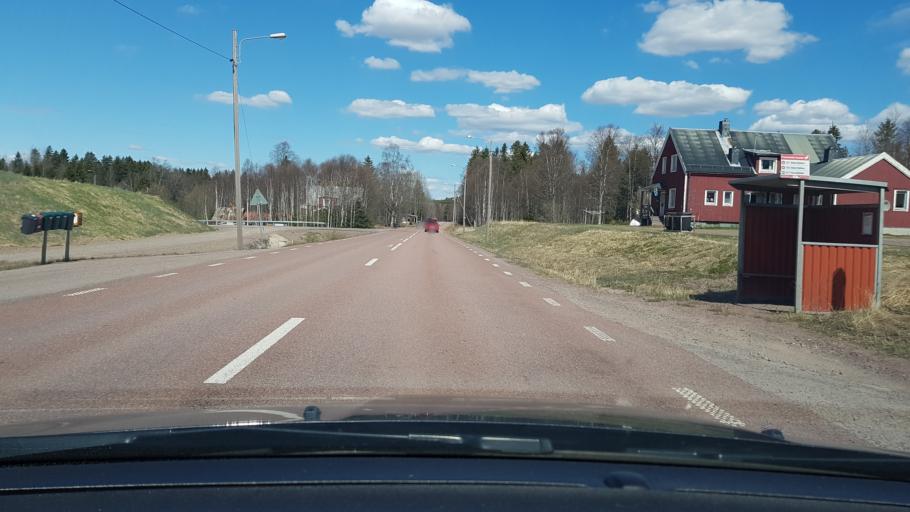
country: SE
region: Dalarna
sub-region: Malung-Saelens kommun
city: Malung
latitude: 61.0701
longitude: 13.3300
